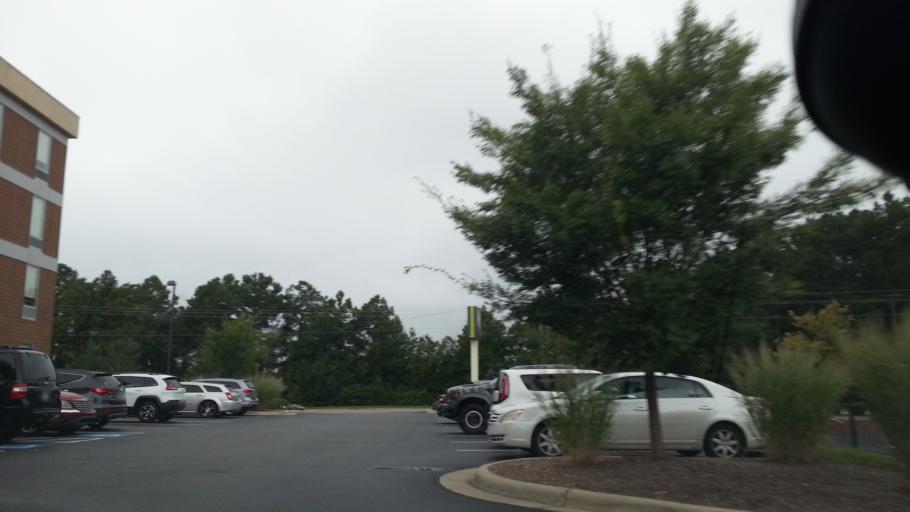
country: US
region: North Carolina
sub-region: Cumberland County
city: Fayetteville
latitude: 35.0741
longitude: -78.9558
